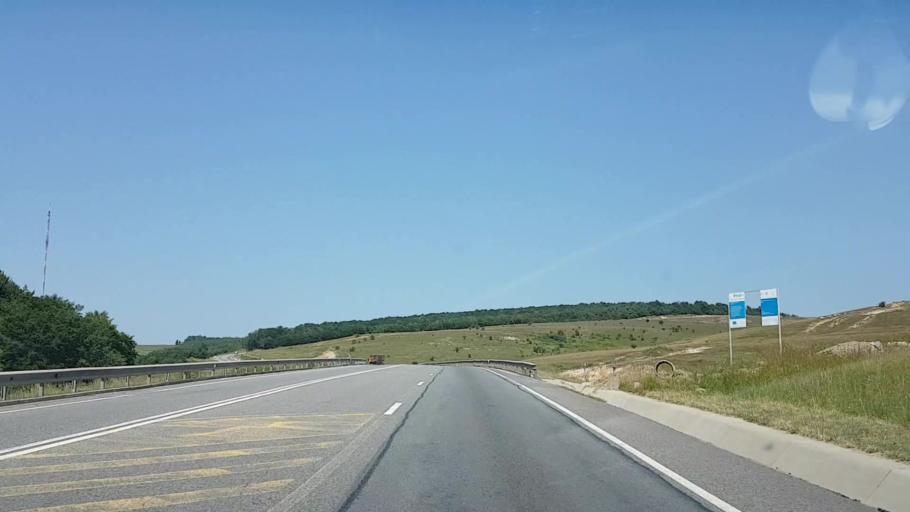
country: RO
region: Cluj
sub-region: Comuna Feleacu
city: Feleacu
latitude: 46.7001
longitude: 23.6399
